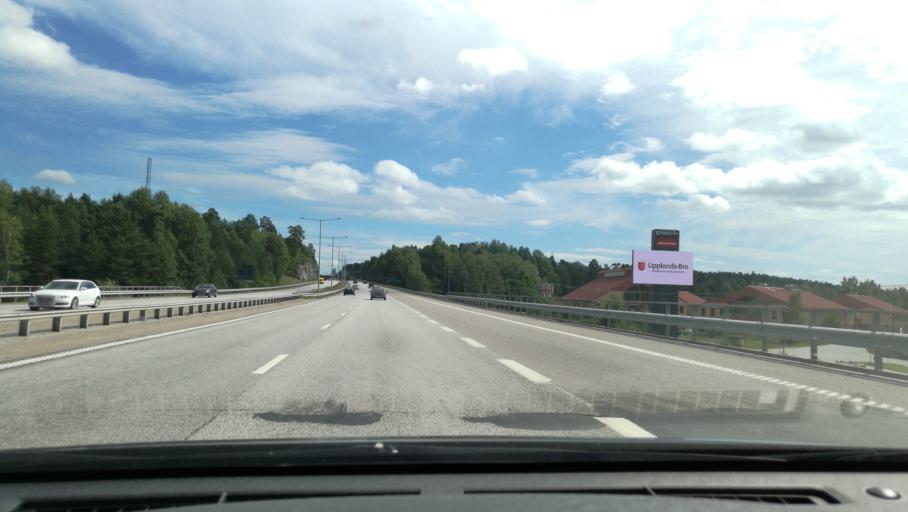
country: SE
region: Stockholm
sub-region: Upplands-Bro Kommun
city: Kungsaengen
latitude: 59.4927
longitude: 17.7480
